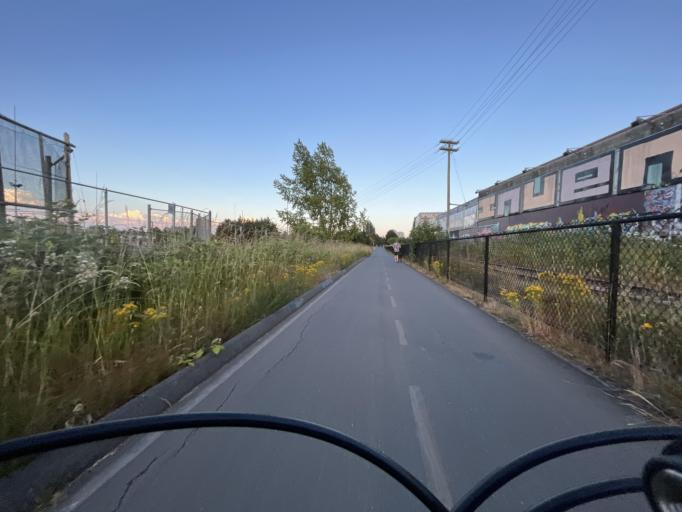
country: CA
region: British Columbia
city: Victoria
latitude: 48.4348
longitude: -123.3956
